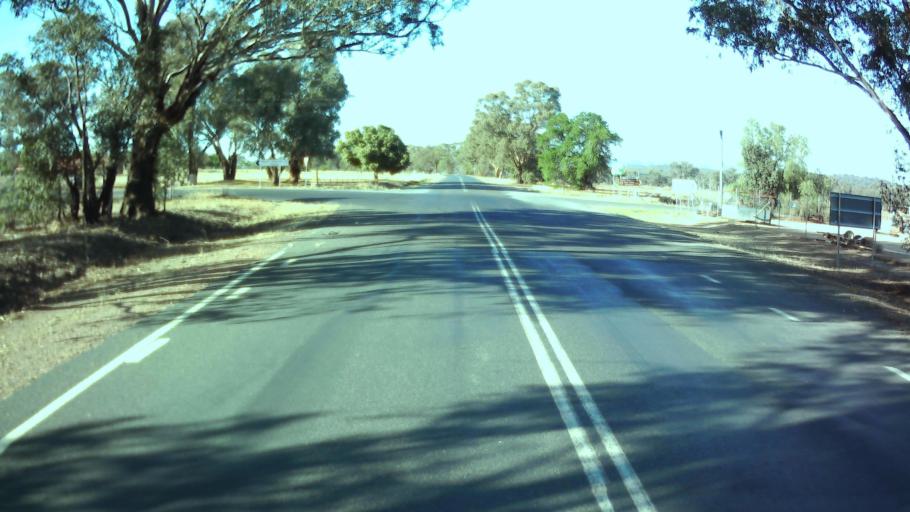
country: AU
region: New South Wales
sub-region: Weddin
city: Grenfell
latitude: -33.9052
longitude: 148.1480
